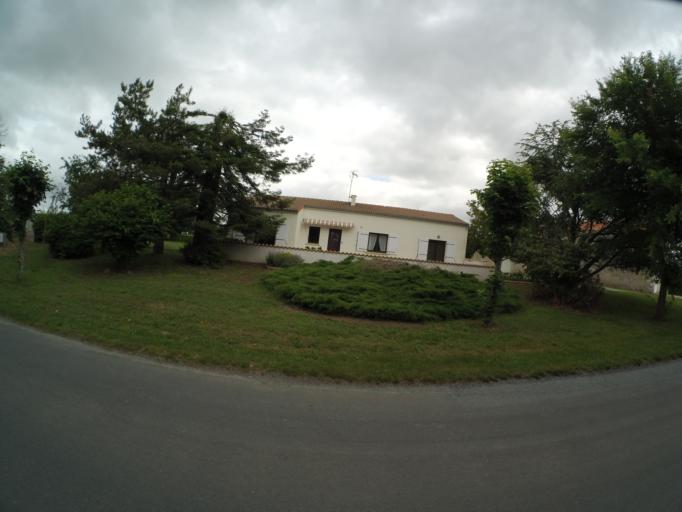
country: FR
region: Poitou-Charentes
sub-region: Departement de la Charente-Maritime
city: Saint-Laurent-de-la-Pree
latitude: 45.9856
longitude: -1.0095
